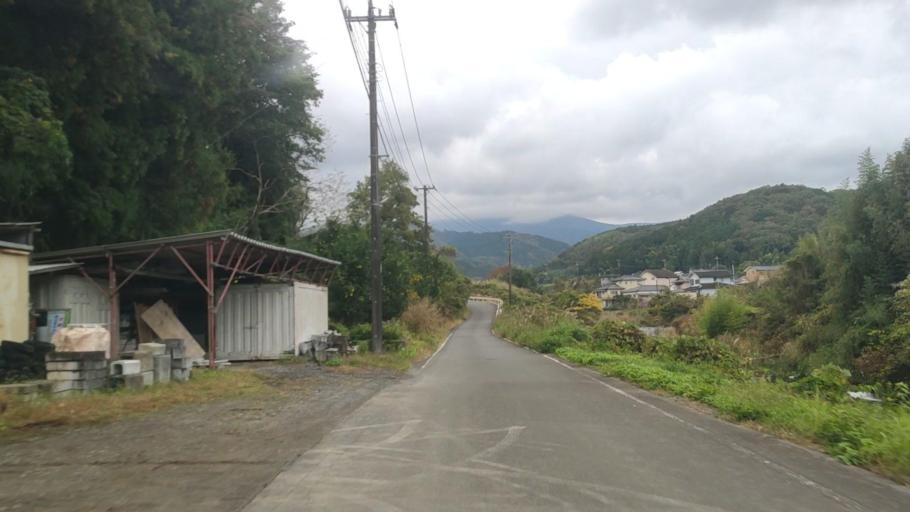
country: JP
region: Shizuoka
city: Ito
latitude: 34.9390
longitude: 138.9985
